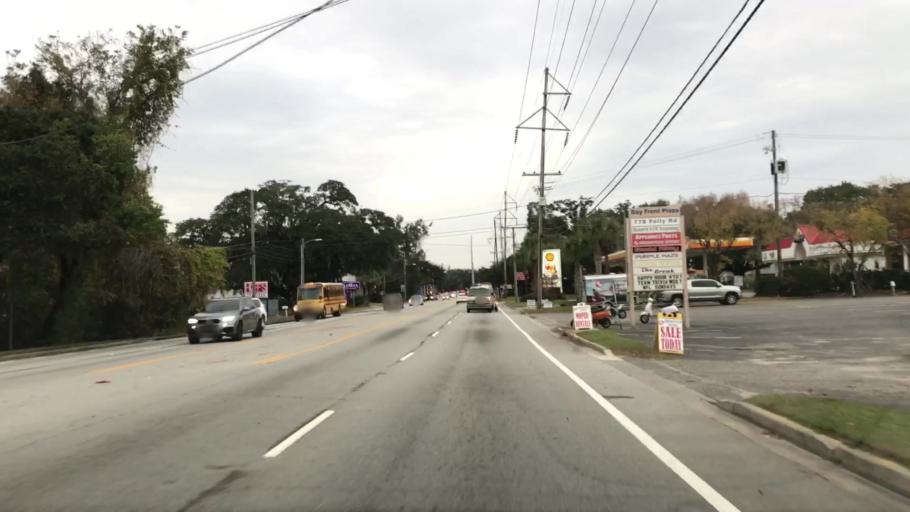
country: US
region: South Carolina
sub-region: Charleston County
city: Charleston
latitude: 32.7408
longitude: -79.9675
